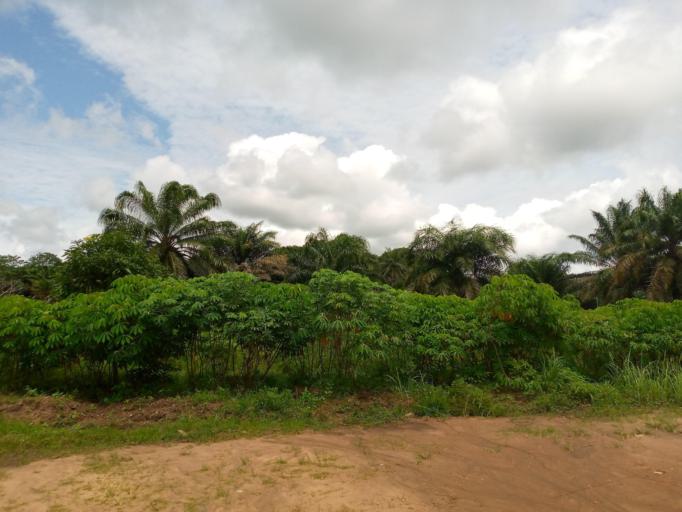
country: SL
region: Northern Province
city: Magburaka
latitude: 8.7167
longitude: -11.9268
